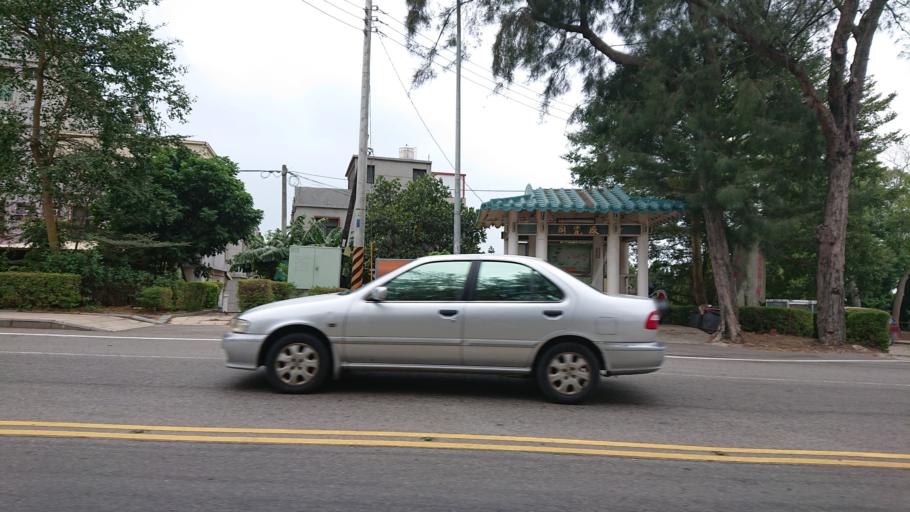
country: TW
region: Fukien
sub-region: Kinmen
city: Jincheng
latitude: 24.4364
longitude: 118.4088
